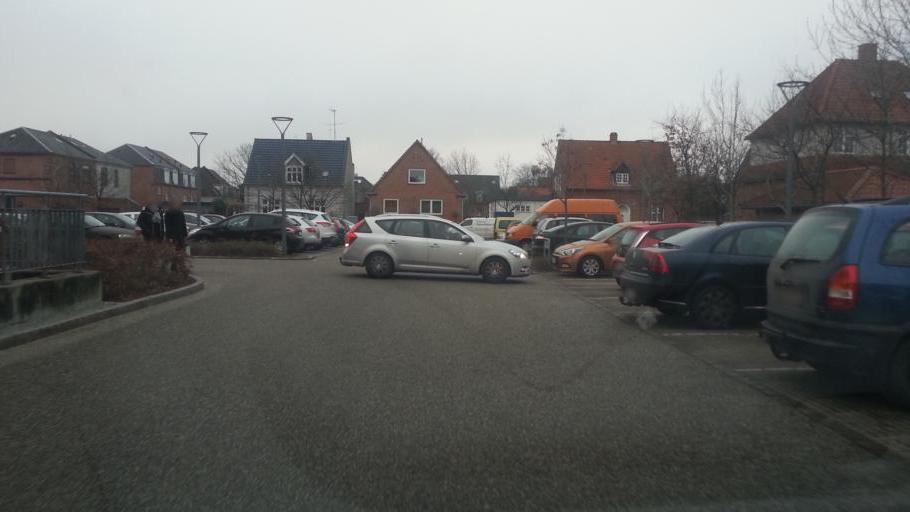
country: DK
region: South Denmark
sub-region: Esbjerg Kommune
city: Esbjerg
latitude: 55.4739
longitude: 8.4558
